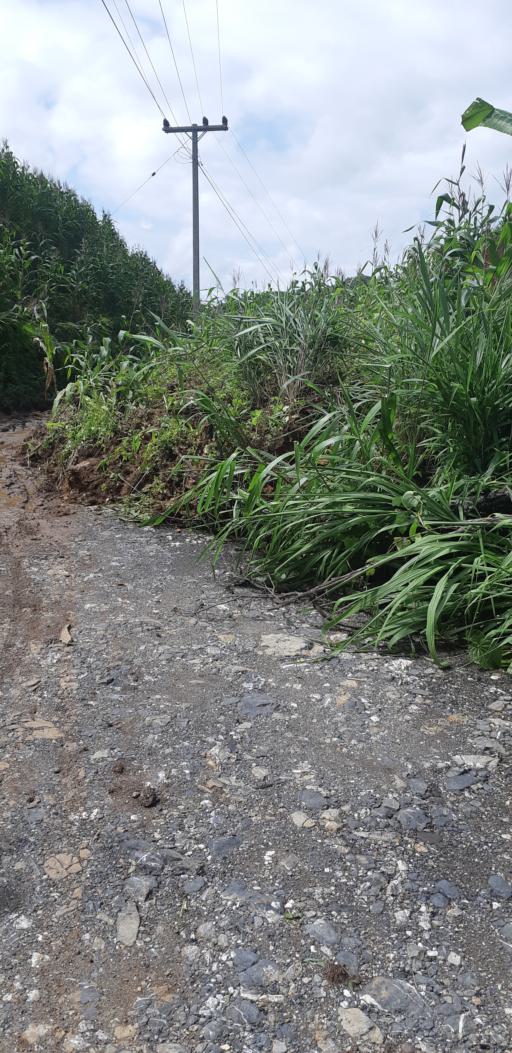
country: LA
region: Loungnamtha
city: Muang Nale
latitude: 20.0325
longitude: 101.5011
